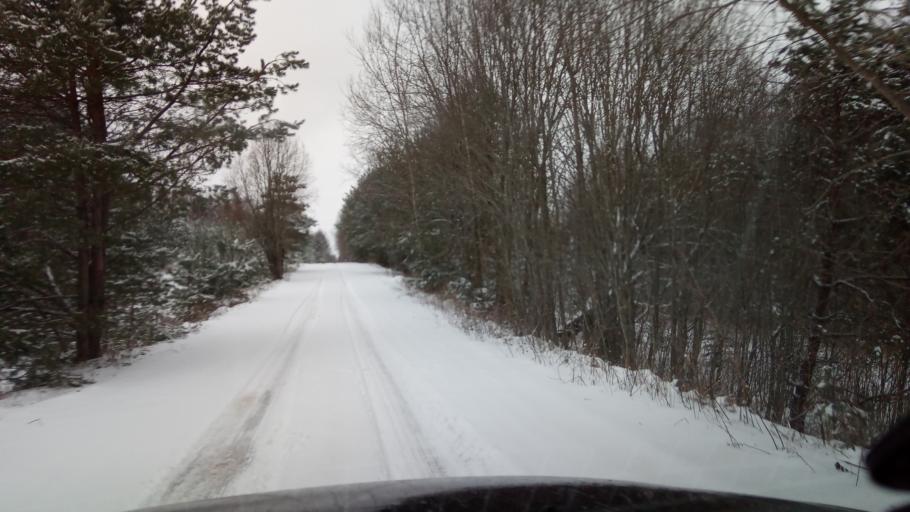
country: LT
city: Zarasai
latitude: 55.6654
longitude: 26.0902
